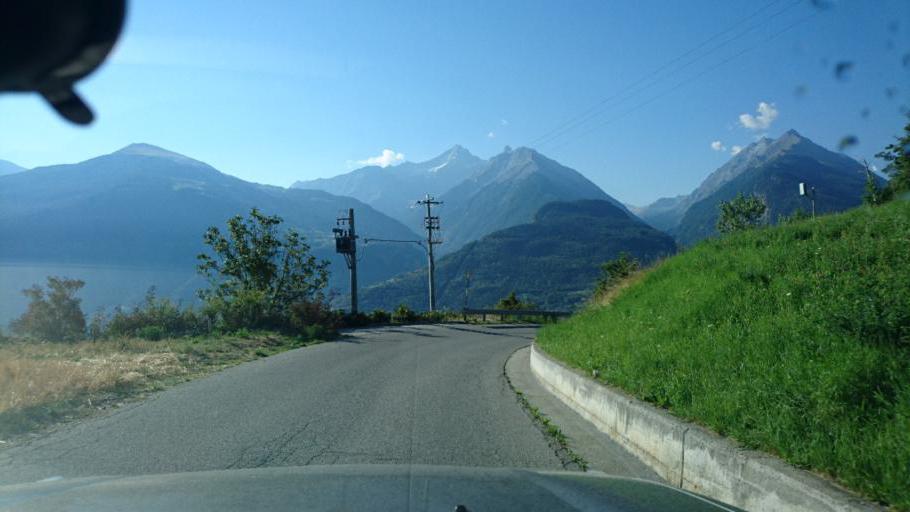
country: IT
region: Aosta Valley
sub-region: Valle d'Aosta
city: Villeneuve
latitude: 45.7178
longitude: 7.2067
